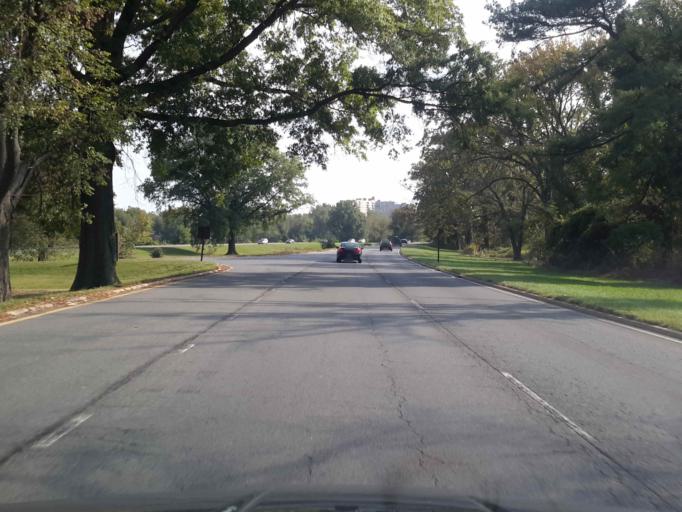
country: US
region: Virginia
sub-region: City of Alexandria
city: Alexandria
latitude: 38.8311
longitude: -77.0441
